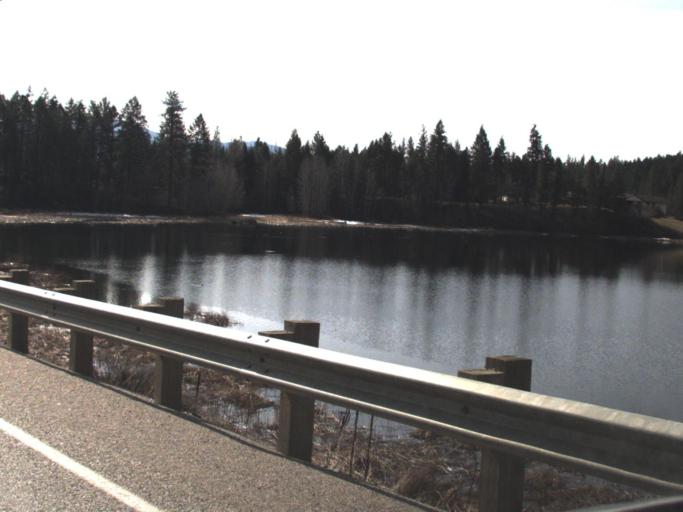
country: US
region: Washington
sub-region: Stevens County
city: Colville
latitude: 48.5205
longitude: -117.8122
